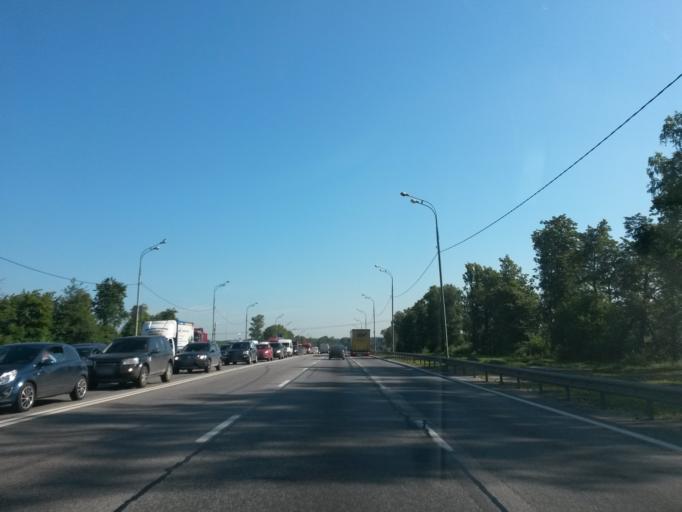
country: RU
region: Moskovskaya
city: Bolshevo
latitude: 55.9516
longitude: 37.8167
